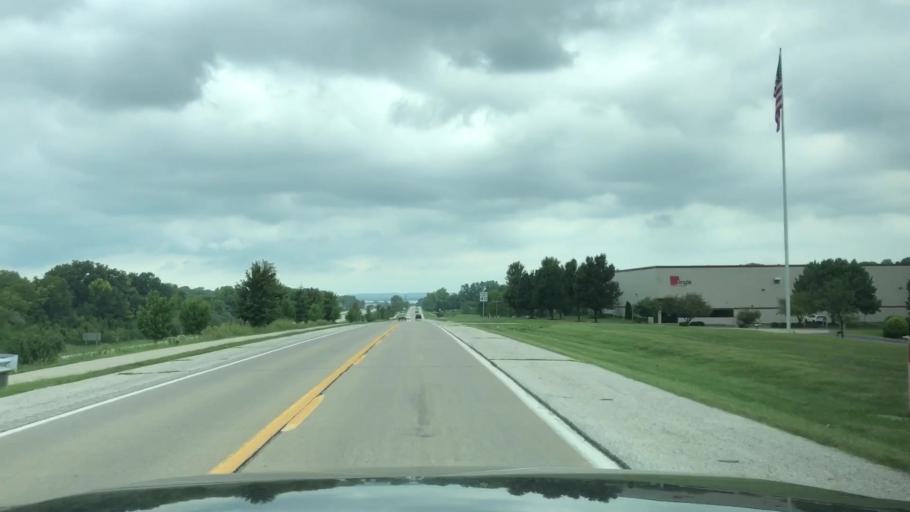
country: US
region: Missouri
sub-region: Saint Charles County
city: Saint Charles
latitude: 38.8091
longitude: -90.4837
